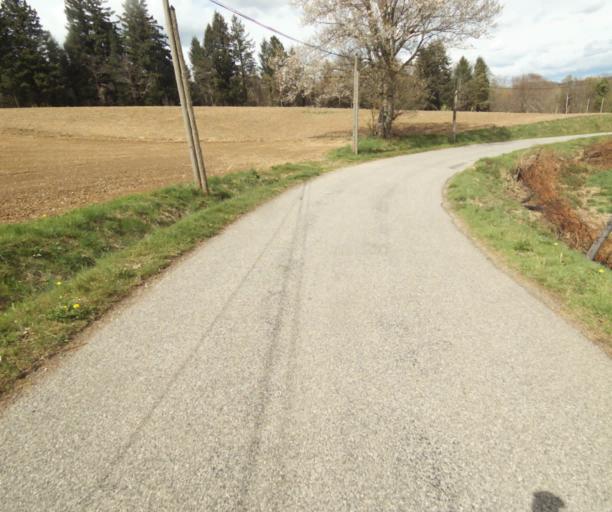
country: FR
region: Limousin
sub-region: Departement de la Correze
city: Laguenne
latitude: 45.2348
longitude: 1.8673
